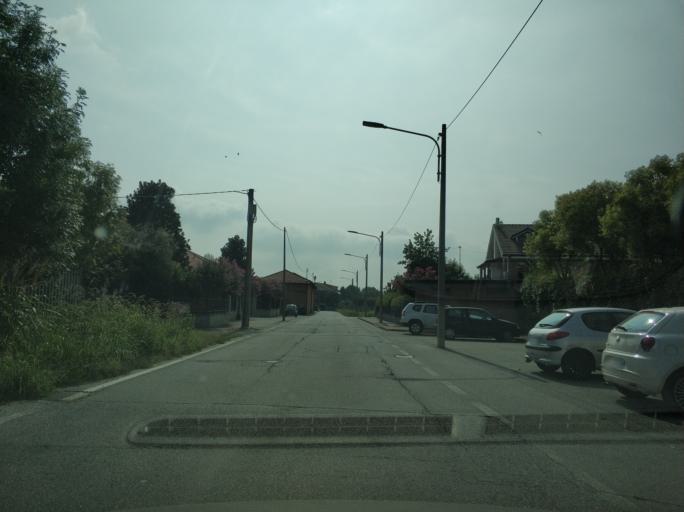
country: IT
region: Piedmont
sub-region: Provincia di Torino
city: San Maurizio
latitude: 45.2000
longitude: 7.6170
